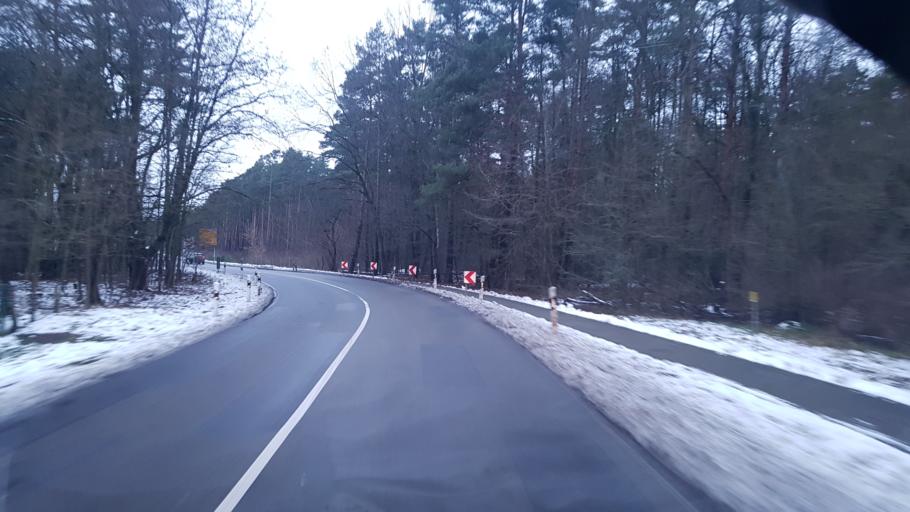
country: DE
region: Brandenburg
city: Mullrose
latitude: 52.2576
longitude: 14.4156
